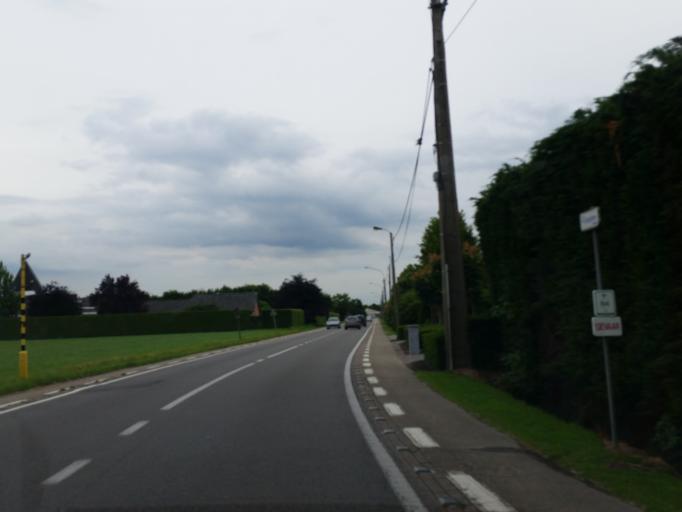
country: BE
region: Flanders
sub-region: Provincie Antwerpen
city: Ranst
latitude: 51.1930
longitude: 4.6038
